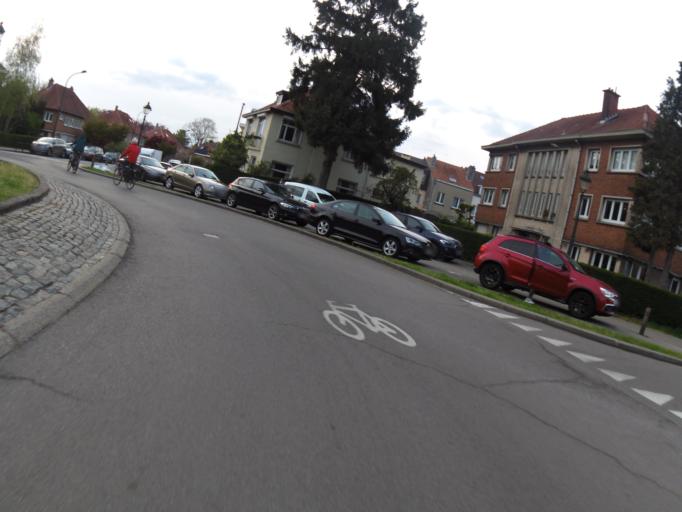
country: BE
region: Flanders
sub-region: Provincie Vlaams-Brabant
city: Kraainem
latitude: 50.8245
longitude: 4.4579
